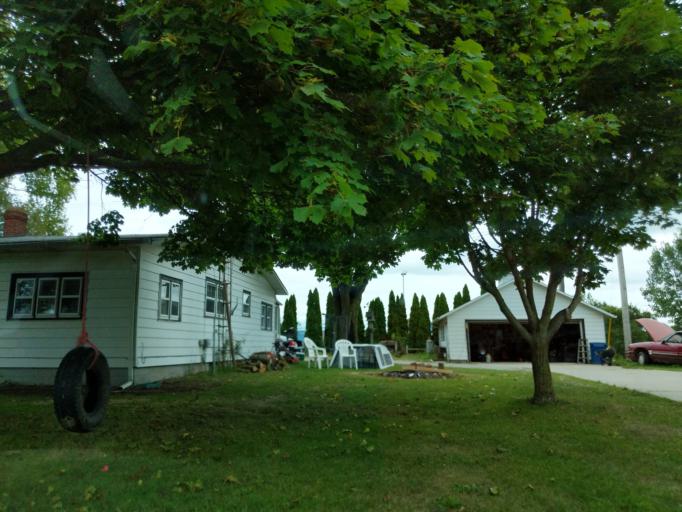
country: US
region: Michigan
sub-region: Lapeer County
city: Barnes Lake-Millers Lake
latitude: 43.3365
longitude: -83.3441
